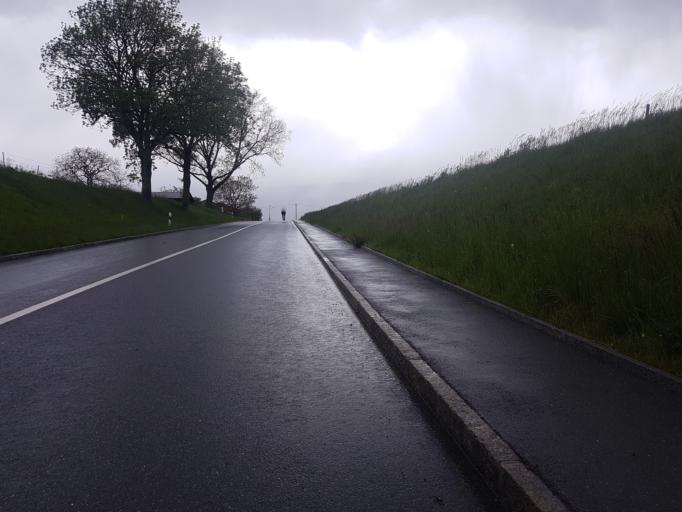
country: CH
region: Geneva
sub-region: Geneva
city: Aire-la-Ville
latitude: 46.1921
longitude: 6.0195
